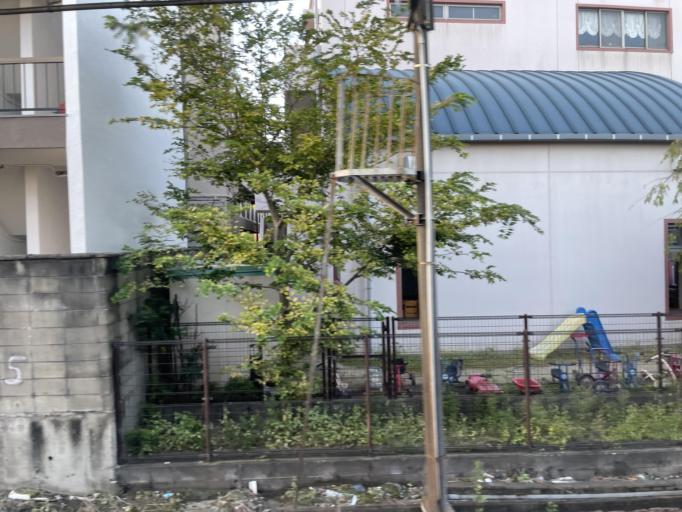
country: JP
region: Osaka
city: Matsubara
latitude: 34.5755
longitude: 135.5541
